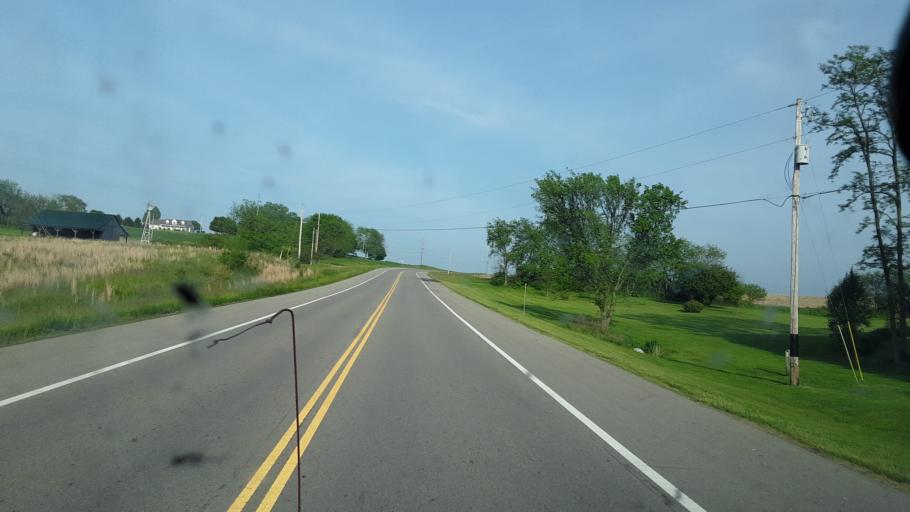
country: US
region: Ohio
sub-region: Ross County
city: Kingston
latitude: 39.5264
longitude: -82.8325
